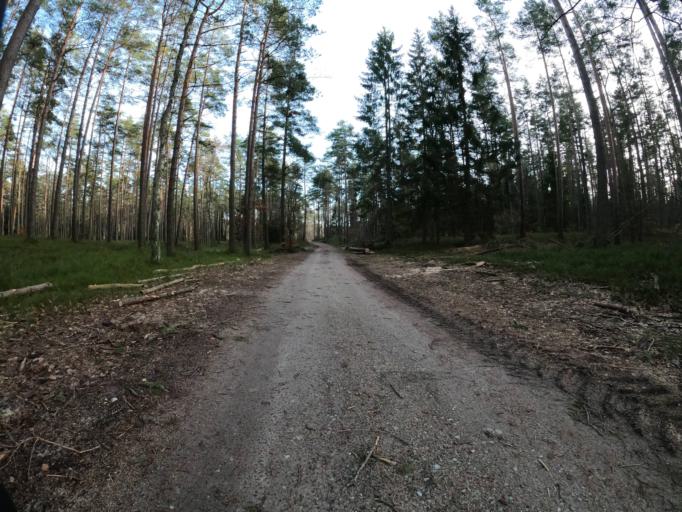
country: PL
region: West Pomeranian Voivodeship
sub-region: Powiat koszalinski
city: Polanow
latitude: 54.1725
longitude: 16.6585
